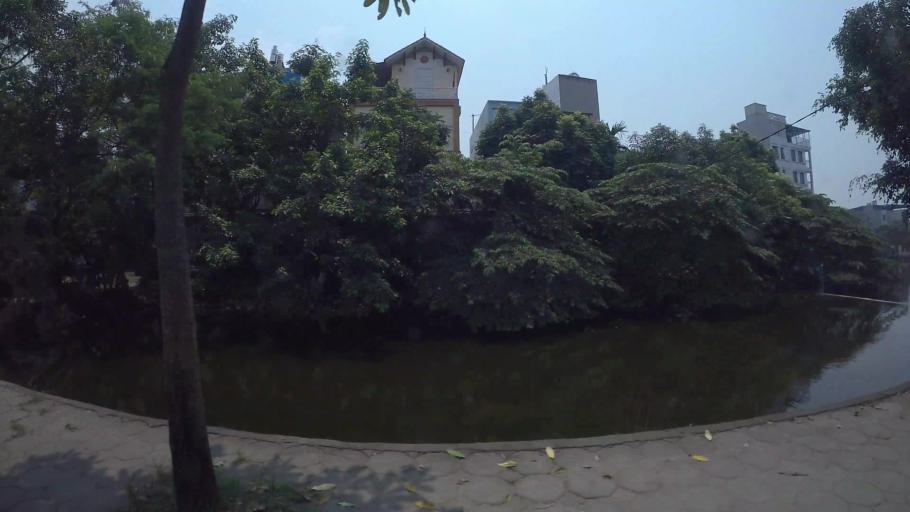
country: VN
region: Ha Noi
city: Van Dien
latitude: 20.9561
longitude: 105.8298
